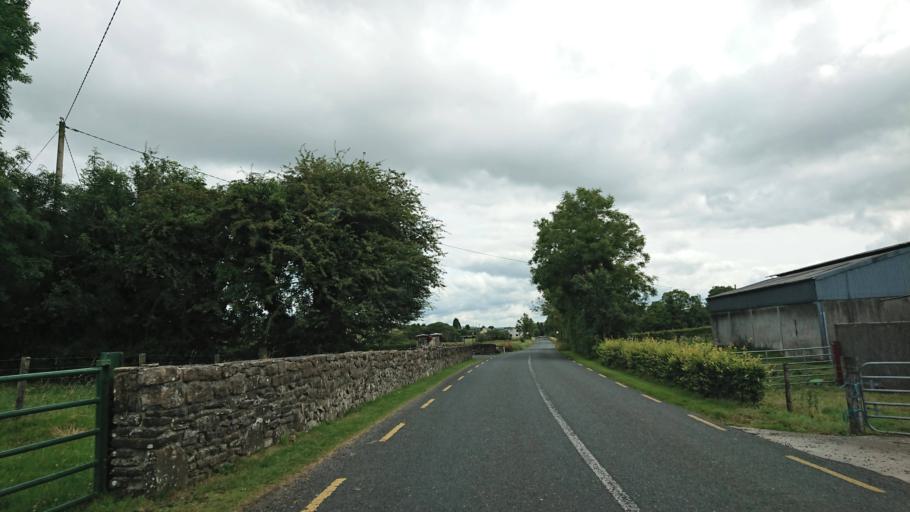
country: IE
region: Connaught
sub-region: County Leitrim
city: Carrick-on-Shannon
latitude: 54.0505
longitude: -8.1300
